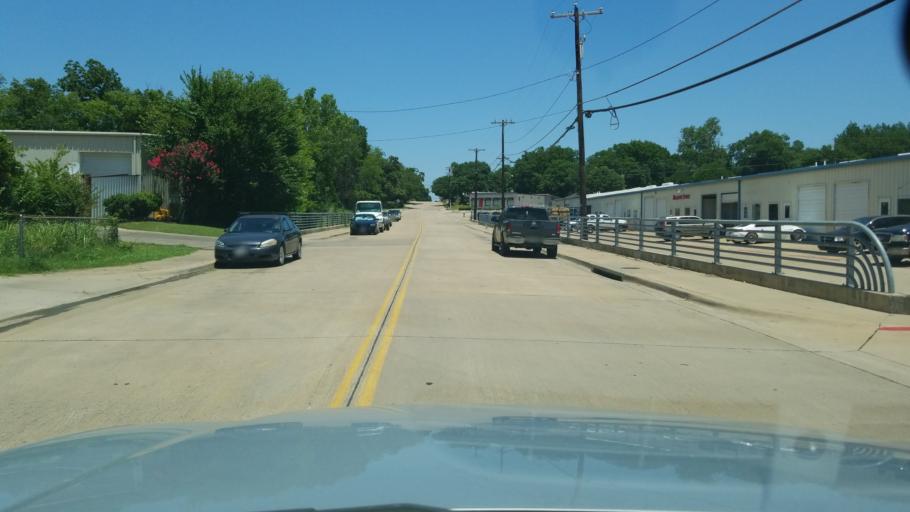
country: US
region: Texas
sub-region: Dallas County
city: Irving
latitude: 32.8023
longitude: -96.9170
